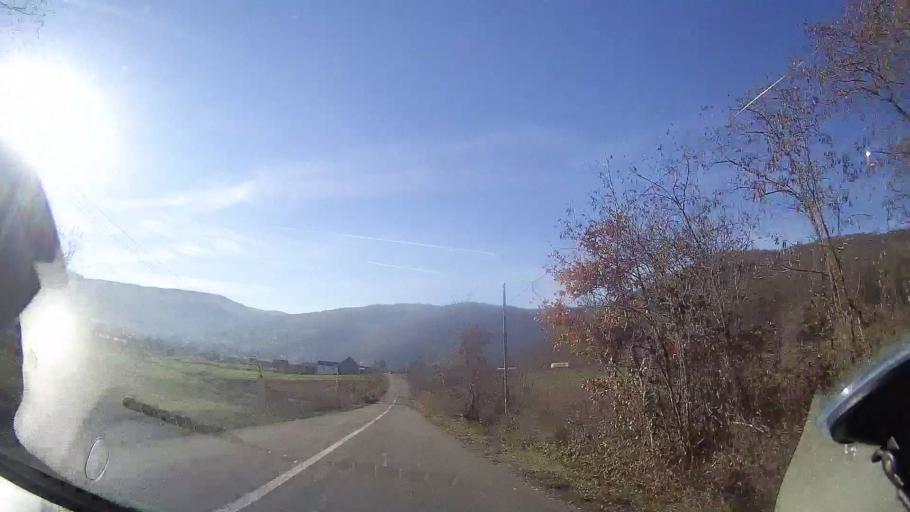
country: RO
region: Bihor
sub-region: Comuna Suncuius
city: Suncuius
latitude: 46.9588
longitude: 22.5420
